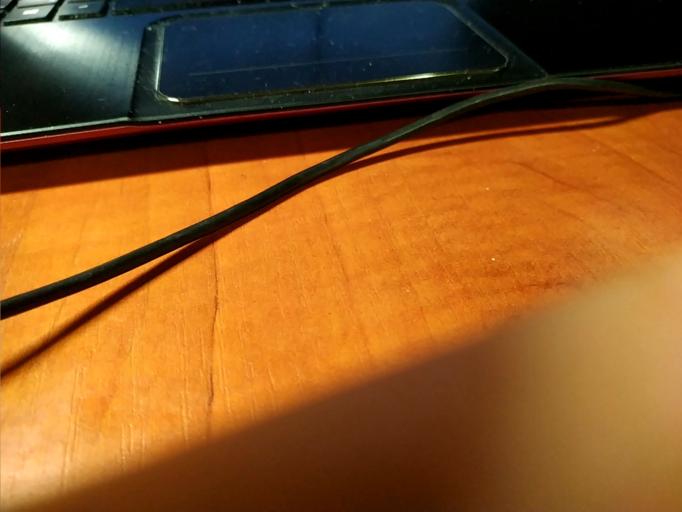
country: RU
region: Tverskaya
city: Rameshki
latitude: 57.1521
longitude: 36.0780
